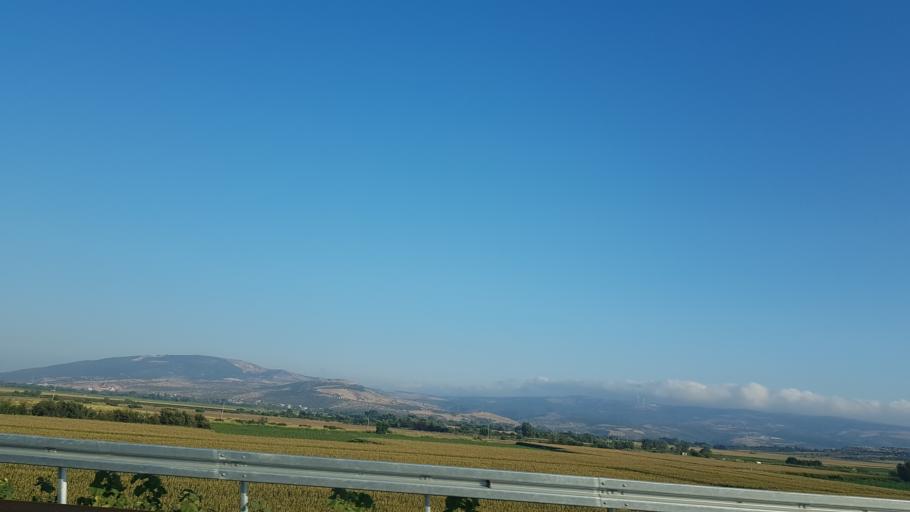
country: TR
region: Bursa
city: Karacabey
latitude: 40.2305
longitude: 28.4136
